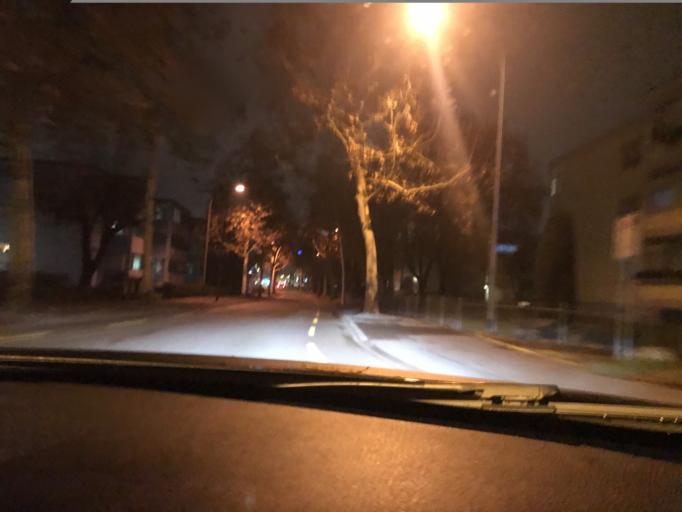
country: CH
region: Zurich
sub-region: Bezirk Buelach
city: Glattbrugg
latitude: 47.4282
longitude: 8.5630
